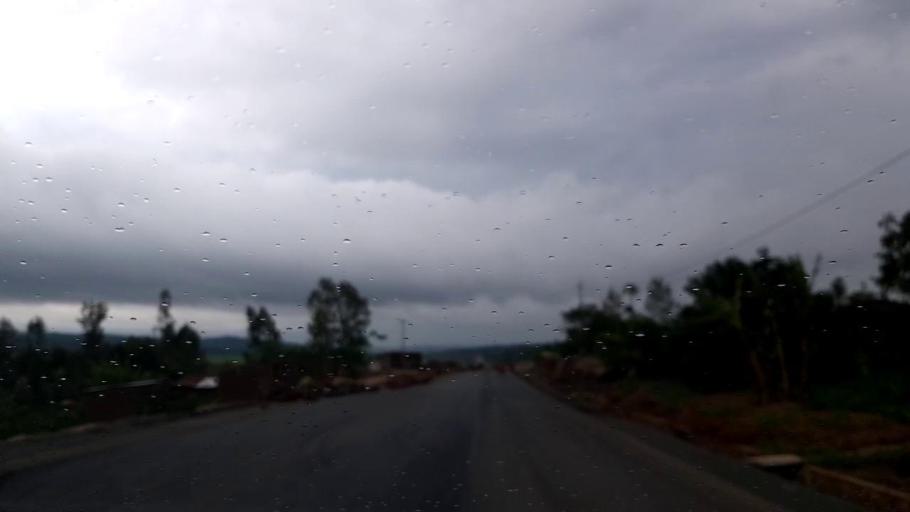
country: RW
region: Northern Province
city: Byumba
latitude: -1.4492
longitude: 30.2461
